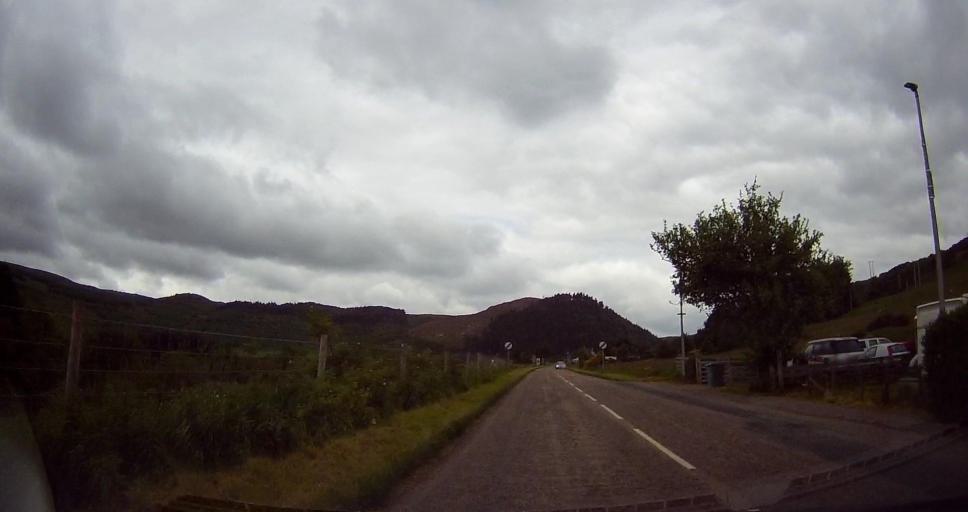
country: GB
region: Scotland
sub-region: Highland
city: Dornoch
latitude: 57.9913
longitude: -4.1644
